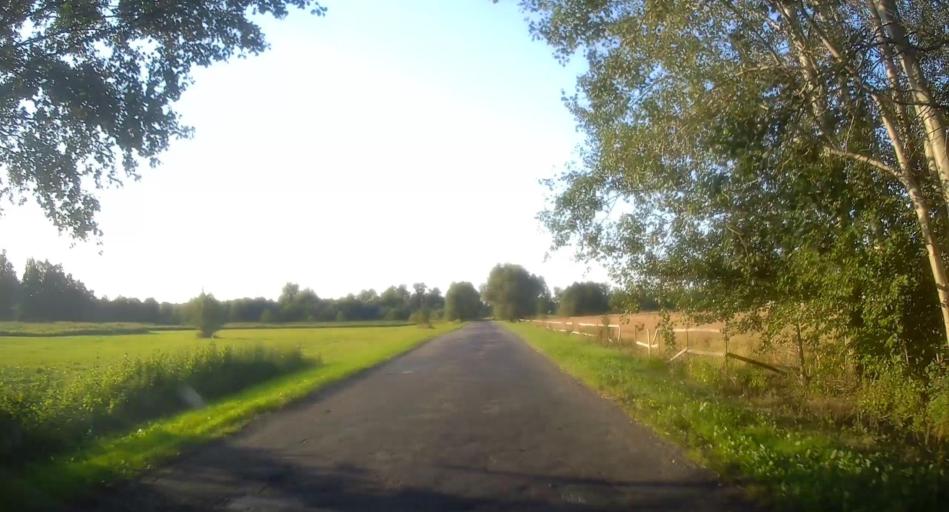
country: PL
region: Lodz Voivodeship
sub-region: Powiat skierniewicki
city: Kaweczyn Nowy
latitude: 51.8975
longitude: 20.2984
